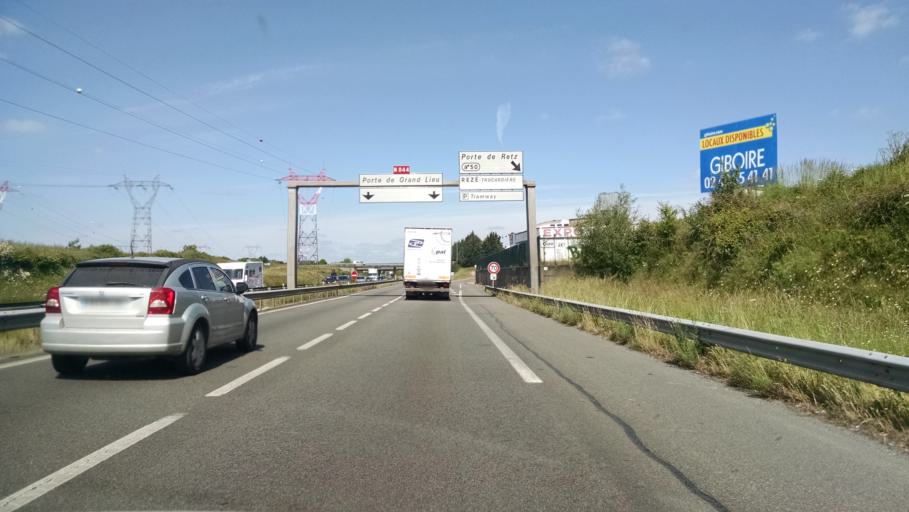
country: FR
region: Pays de la Loire
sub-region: Departement de la Loire-Atlantique
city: Reze
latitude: 47.1677
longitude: -1.5752
